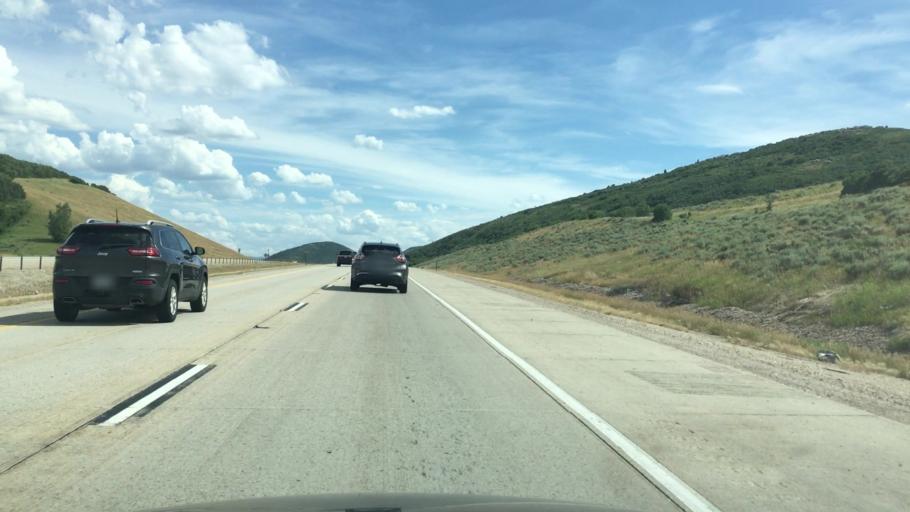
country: US
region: Utah
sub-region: Summit County
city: Park City
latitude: 40.6575
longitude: -111.4577
